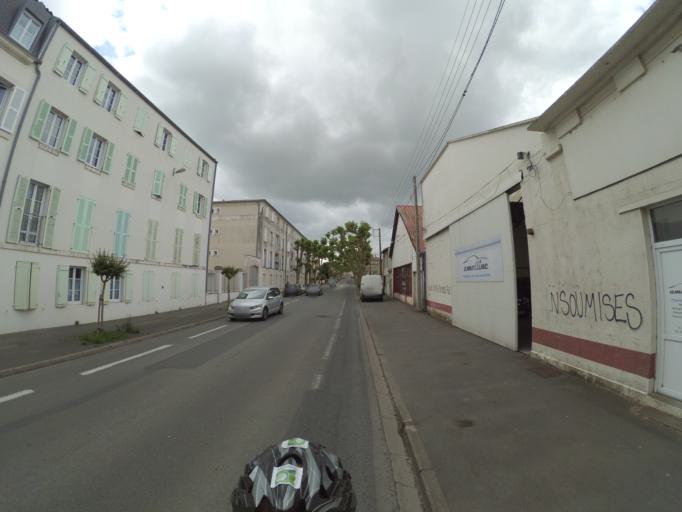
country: FR
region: Poitou-Charentes
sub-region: Departement de la Charente-Maritime
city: Rochefort
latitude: 45.9452
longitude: -0.9622
